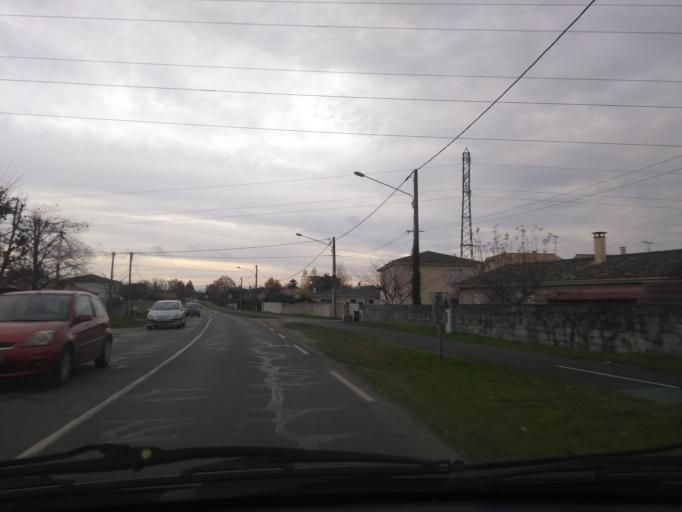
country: FR
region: Aquitaine
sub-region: Departement de la Gironde
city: Leognan
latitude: 44.7403
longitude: -0.6175
